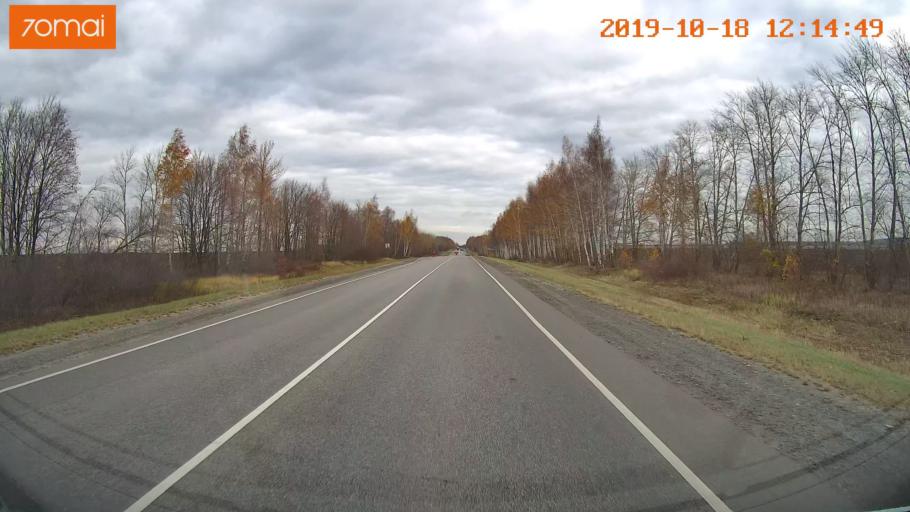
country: RU
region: Rjazan
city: Zakharovo
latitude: 54.4357
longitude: 39.3897
